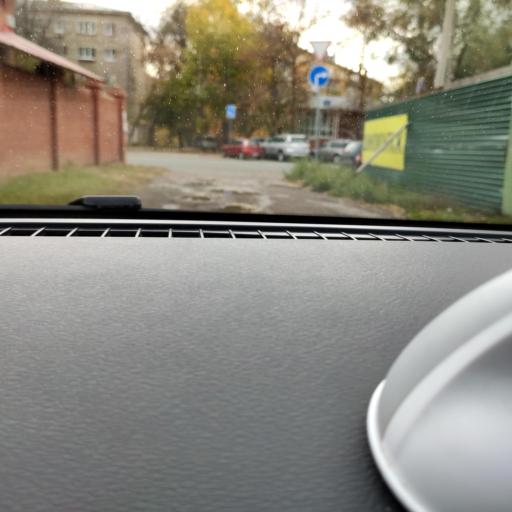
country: RU
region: Samara
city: Samara
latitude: 53.1975
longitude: 50.1962
